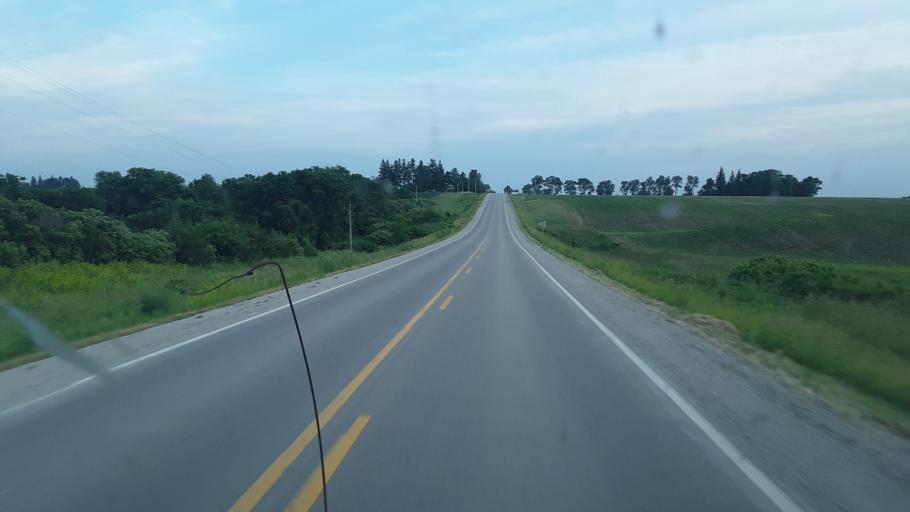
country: US
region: Iowa
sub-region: Iowa County
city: Marengo
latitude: 41.7129
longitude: -92.1828
